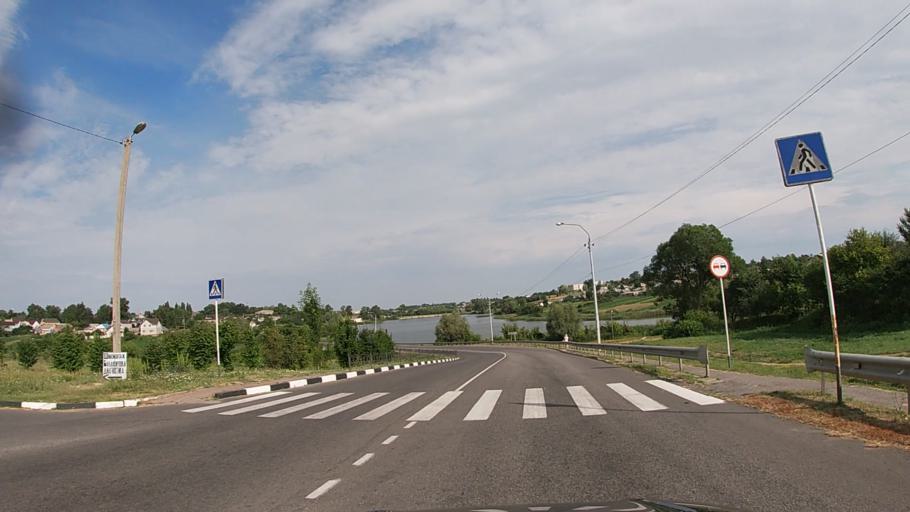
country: RU
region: Belgorod
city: Krasnaya Yaruga
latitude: 50.8006
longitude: 35.6721
